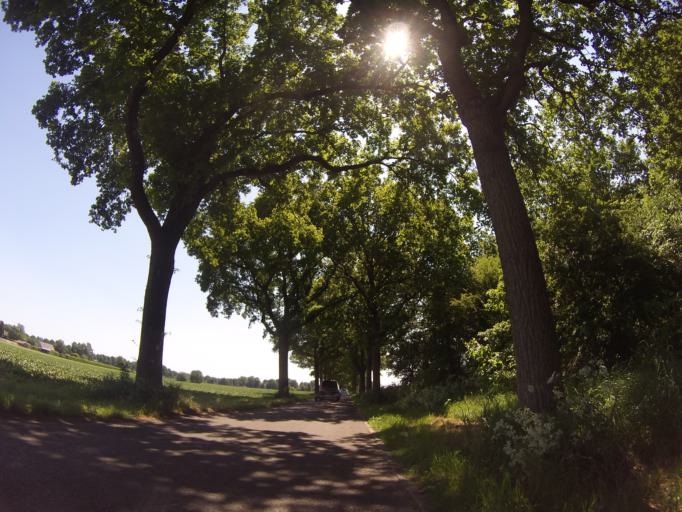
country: NL
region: Drenthe
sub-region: Gemeente Coevorden
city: Sleen
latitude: 52.7309
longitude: 6.8511
